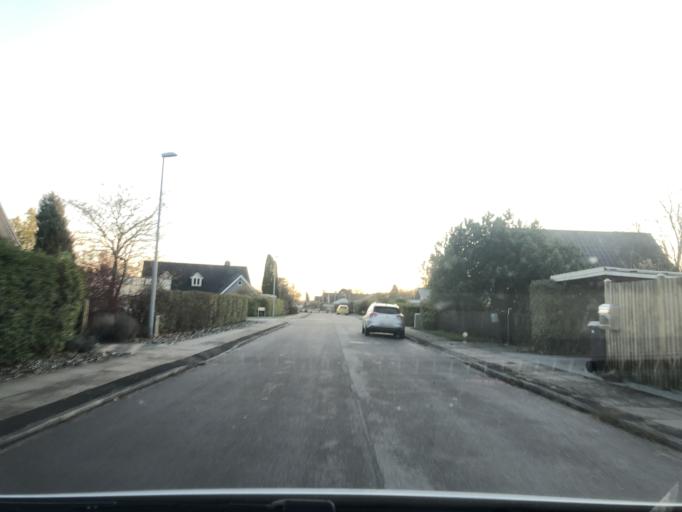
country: DK
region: Capital Region
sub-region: Tarnby Kommune
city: Tarnby
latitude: 55.5998
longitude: 12.5770
